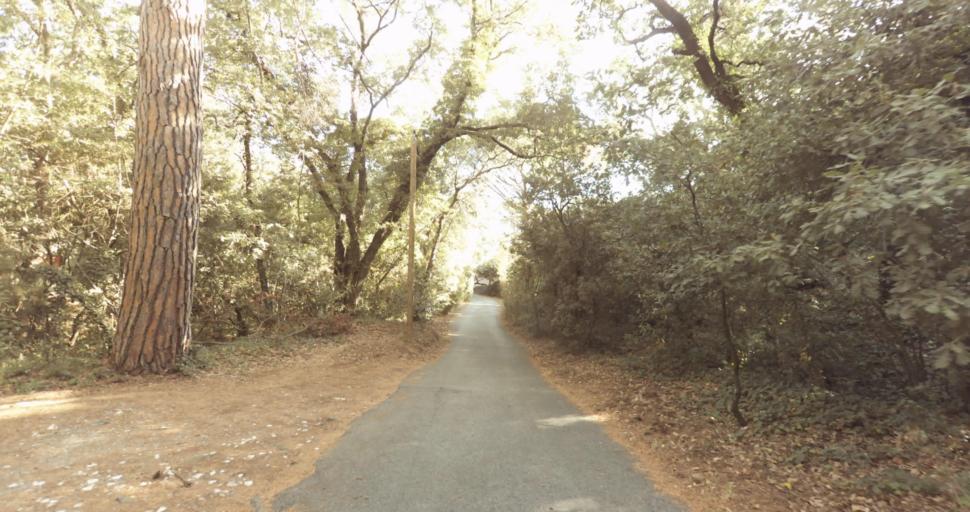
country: FR
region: Provence-Alpes-Cote d'Azur
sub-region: Departement du Var
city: Saint-Tropez
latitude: 43.2557
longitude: 6.6272
